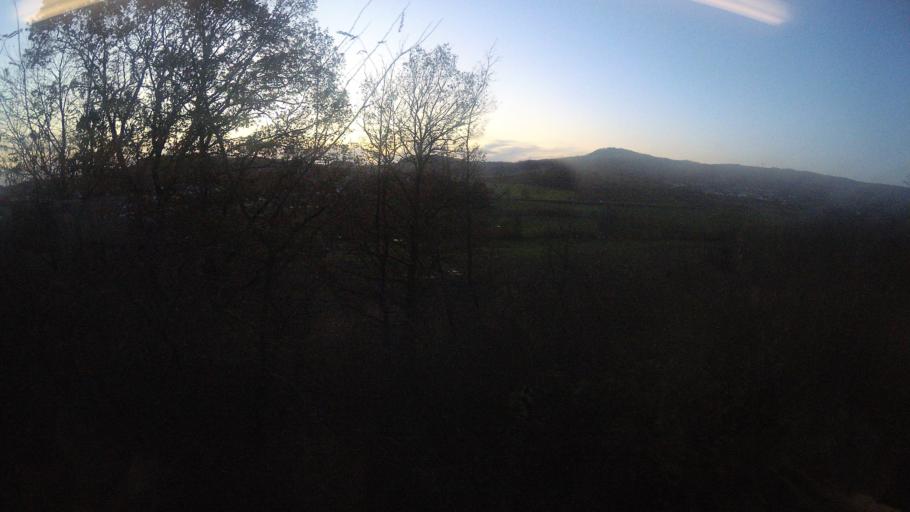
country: DE
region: Rheinland-Pfalz
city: Herchweiler
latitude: 49.5170
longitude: 7.2770
